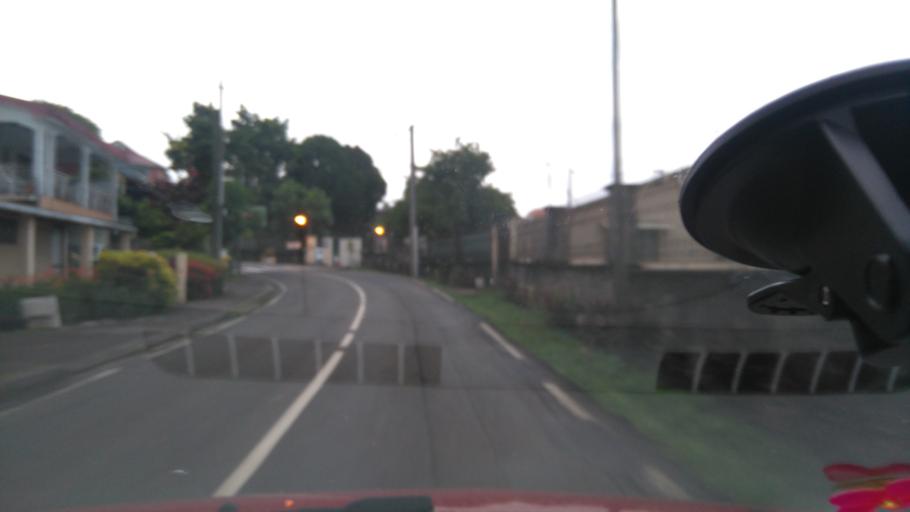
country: MQ
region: Martinique
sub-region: Martinique
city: Saint-Esprit
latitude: 14.5588
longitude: -60.9426
